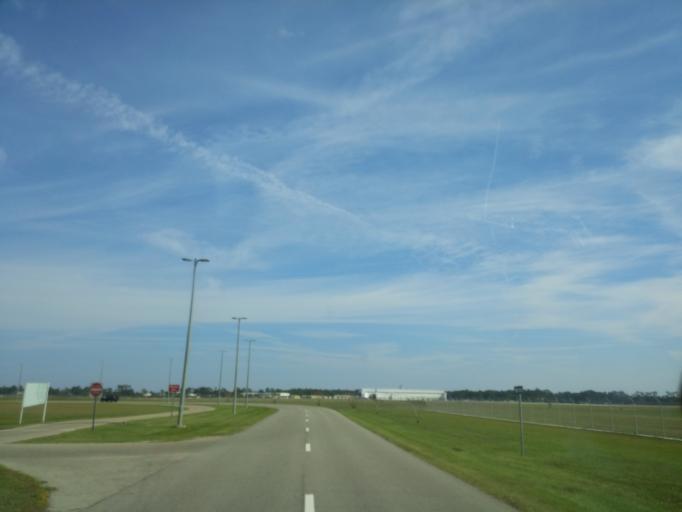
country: US
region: Mississippi
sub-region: Harrison County
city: West Gulfport
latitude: 30.4119
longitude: -89.0695
